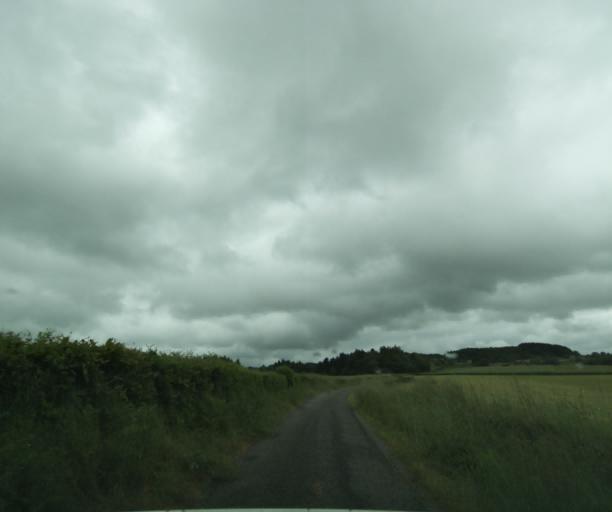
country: FR
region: Bourgogne
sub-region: Departement de Saone-et-Loire
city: Matour
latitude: 46.4418
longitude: 4.4436
